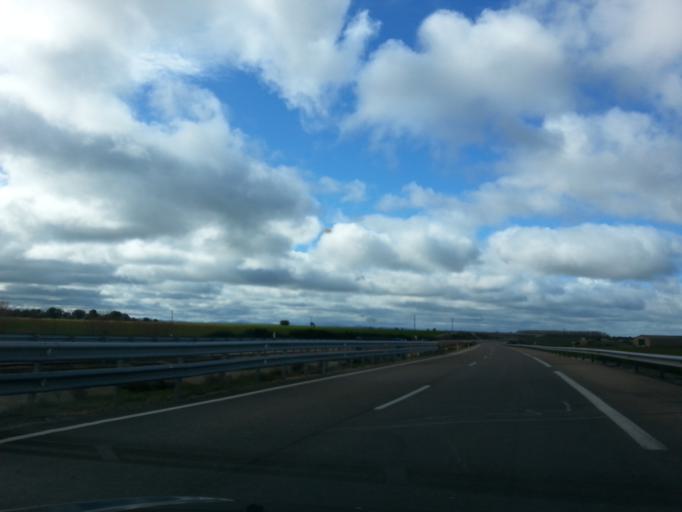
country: ES
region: Castille and Leon
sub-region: Provincia de Salamanca
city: Galindo y Perahuy
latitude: 40.9138
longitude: -5.8630
